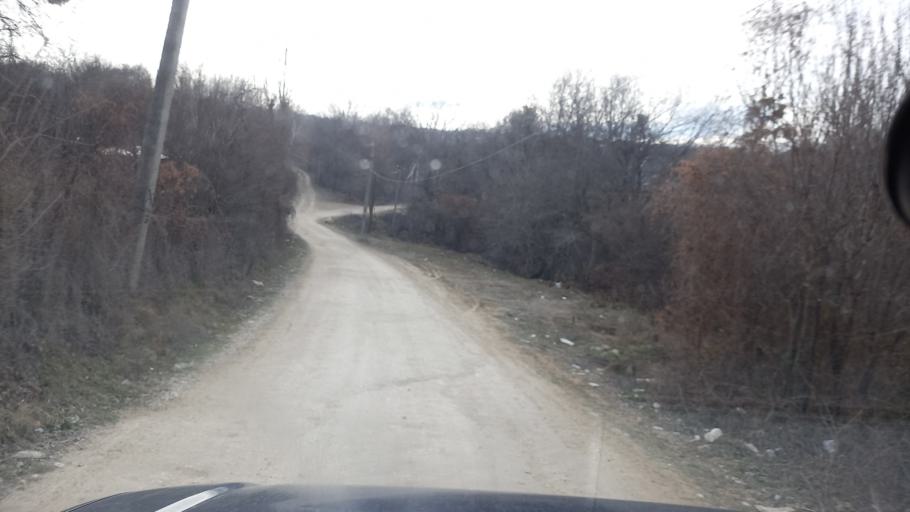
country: RU
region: Adygeya
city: Kamennomostskiy
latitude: 44.2891
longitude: 40.1911
